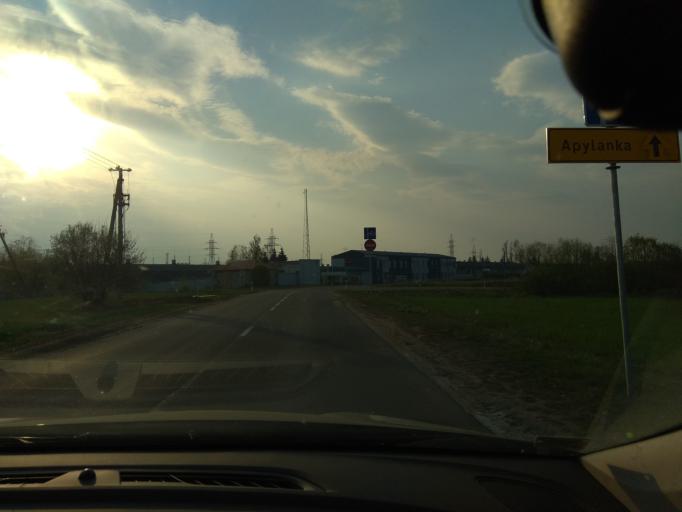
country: LT
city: Baltoji Voke
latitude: 54.6110
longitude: 25.1226
